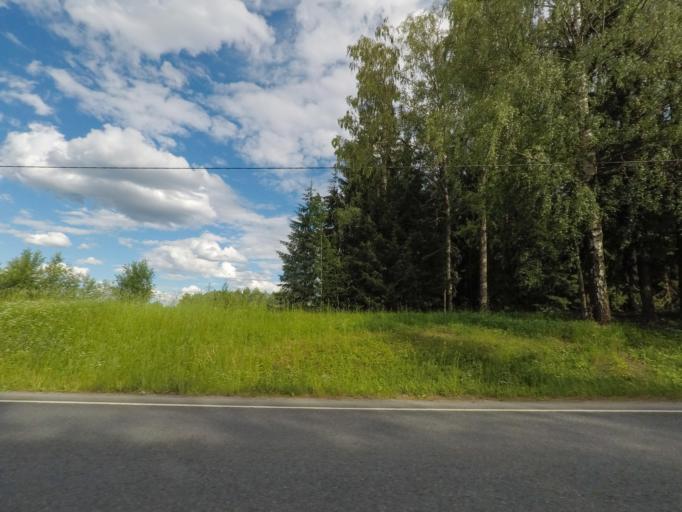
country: FI
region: Paijanne Tavastia
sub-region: Lahti
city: Lahti
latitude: 60.9581
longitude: 25.6200
